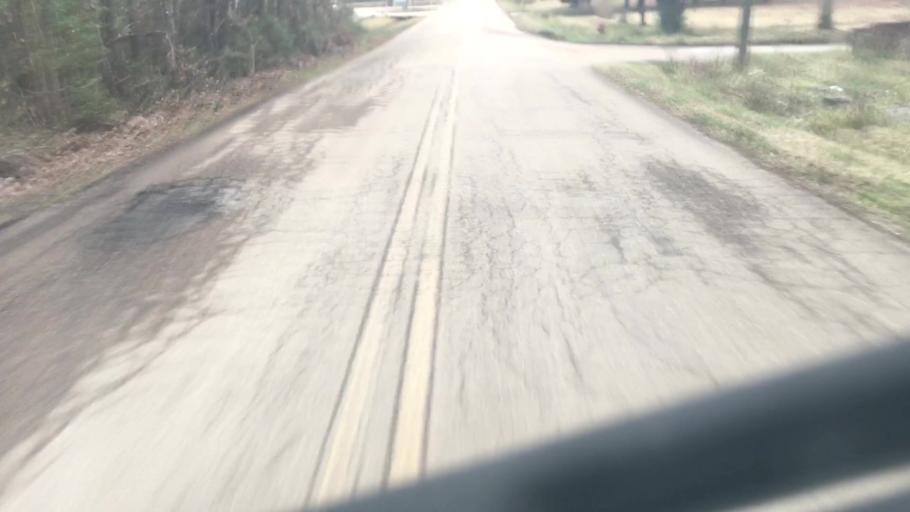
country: US
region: Alabama
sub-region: Walker County
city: Jasper
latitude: 33.8323
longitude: -87.2254
